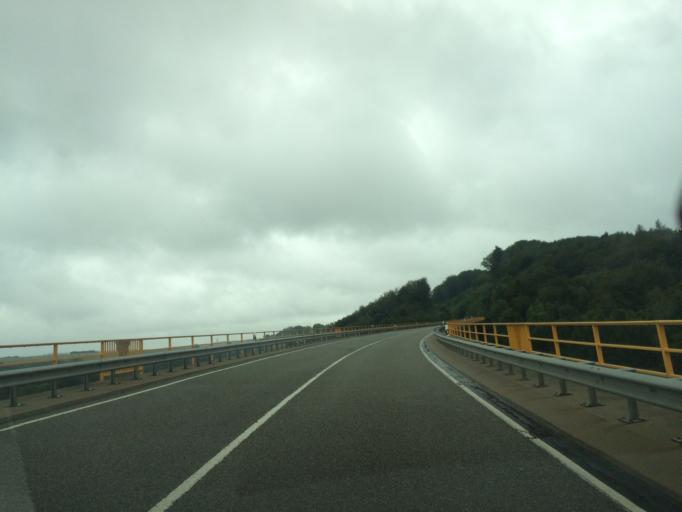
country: DE
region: Rheinland-Pfalz
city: Hoheischweiler
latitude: 49.2191
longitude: 7.5522
